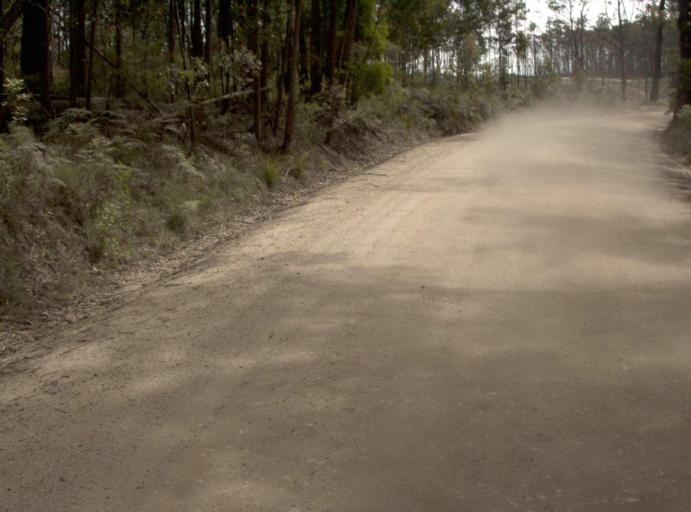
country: AU
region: Victoria
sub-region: East Gippsland
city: Lakes Entrance
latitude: -37.6361
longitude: 148.6706
